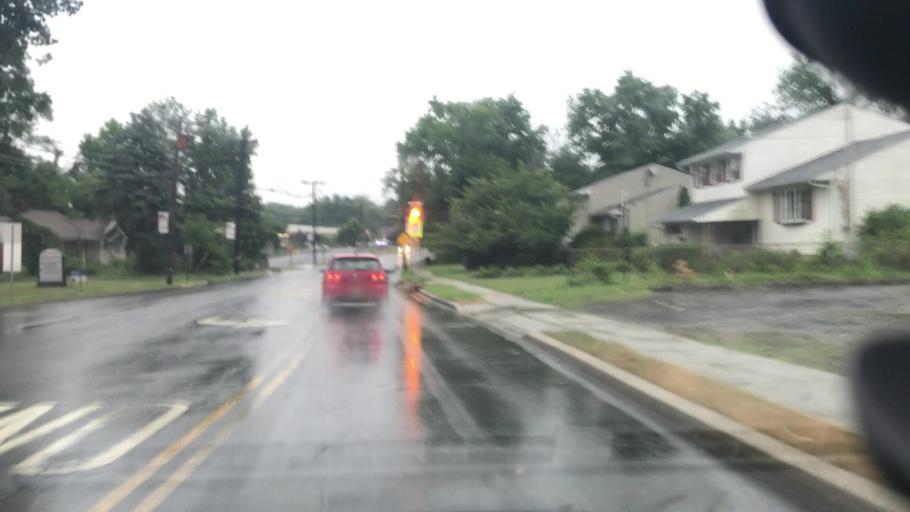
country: US
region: New Jersey
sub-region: Union County
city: Clark
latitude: 40.6257
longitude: -74.3166
